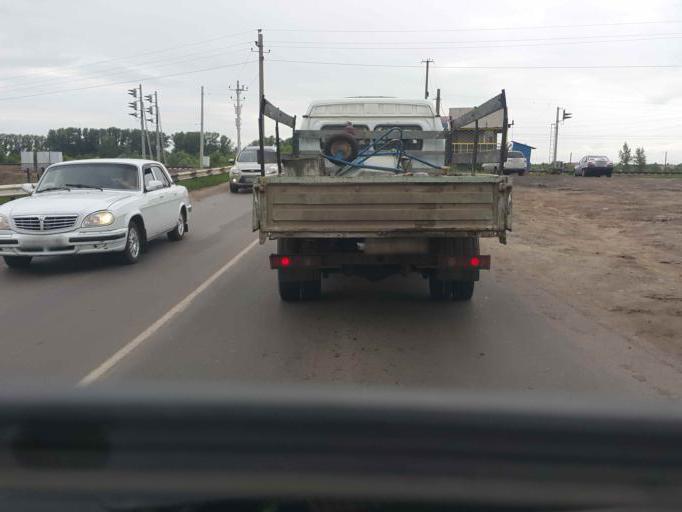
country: RU
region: Tambov
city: Michurinsk
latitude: 52.9168
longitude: 40.5082
